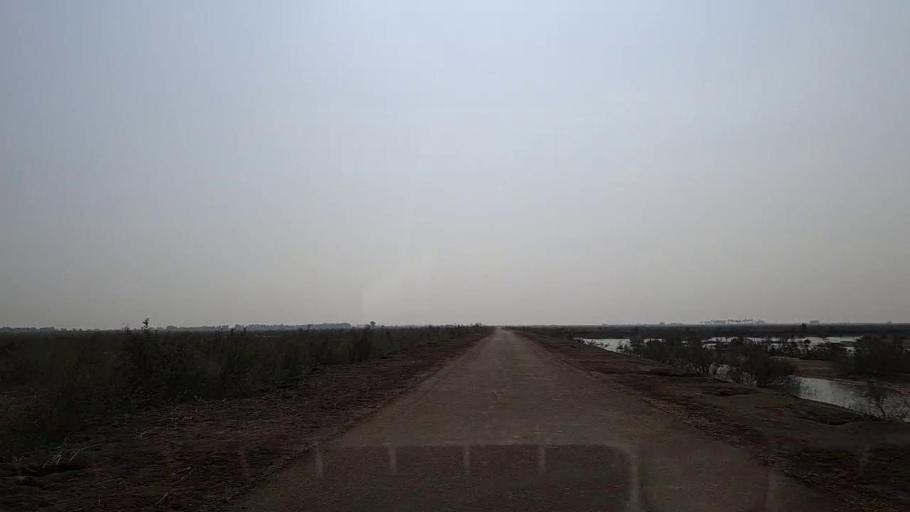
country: PK
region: Sindh
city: Gharo
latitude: 24.6691
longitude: 67.6956
